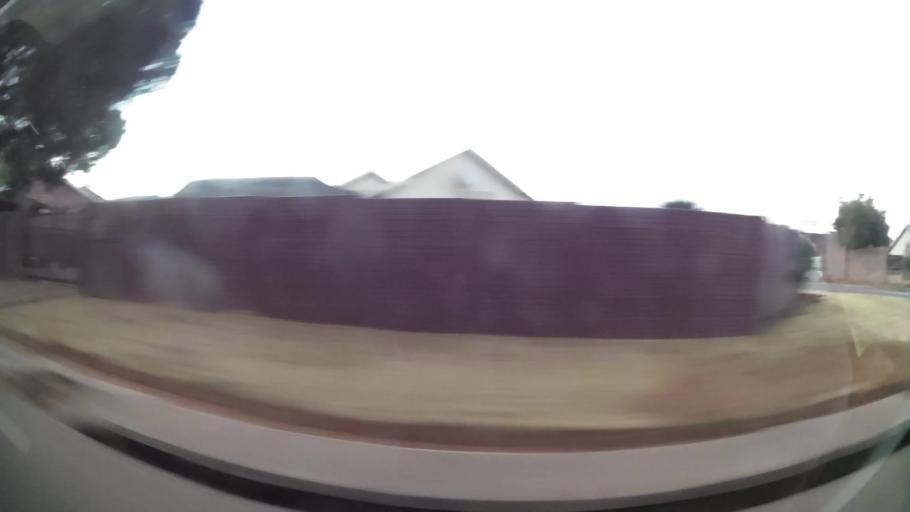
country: ZA
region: Orange Free State
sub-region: Mangaung Metropolitan Municipality
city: Bloemfontein
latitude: -29.1656
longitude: 26.1995
